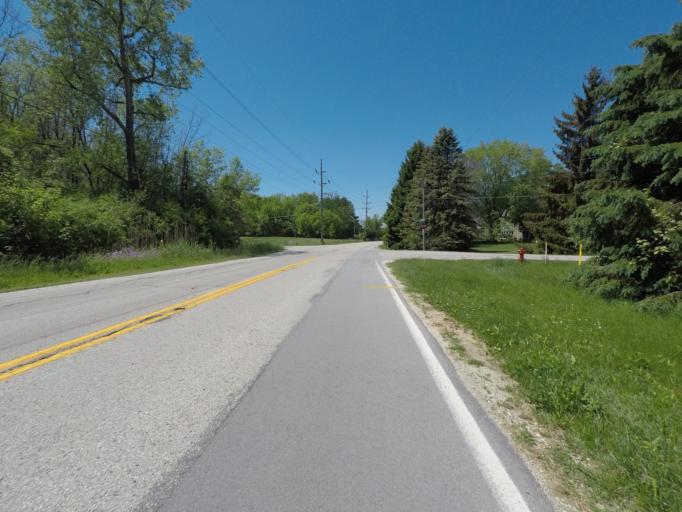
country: US
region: Wisconsin
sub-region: Sheboygan County
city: Kohler
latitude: 43.7510
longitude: -87.7573
